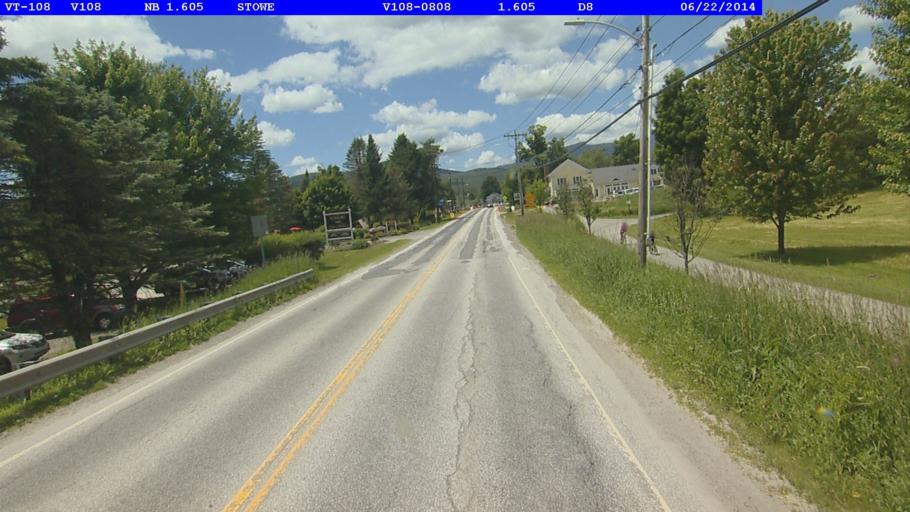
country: US
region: Vermont
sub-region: Lamoille County
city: Morristown
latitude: 44.4726
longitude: -72.7081
